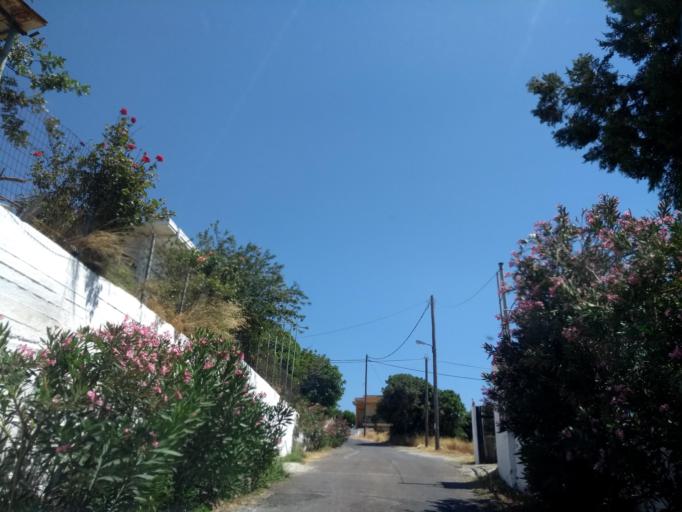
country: GR
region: Crete
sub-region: Nomos Chanias
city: Vryses
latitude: 35.3613
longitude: 23.5339
